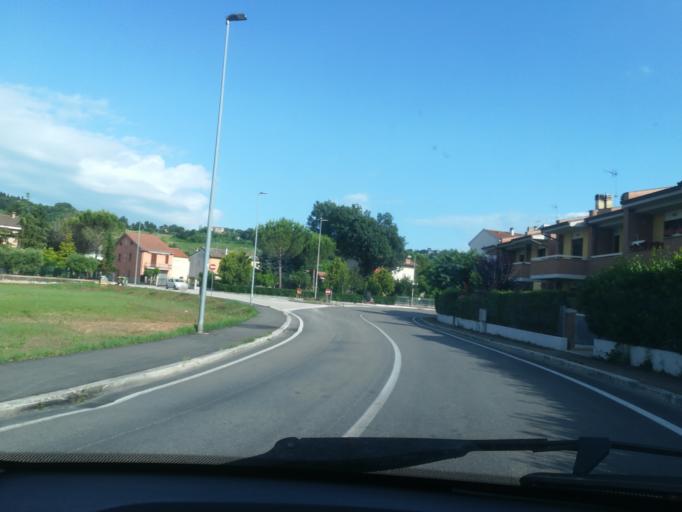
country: IT
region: The Marches
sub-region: Provincia di Macerata
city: Villa Potenza
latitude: 43.3216
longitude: 13.4243
